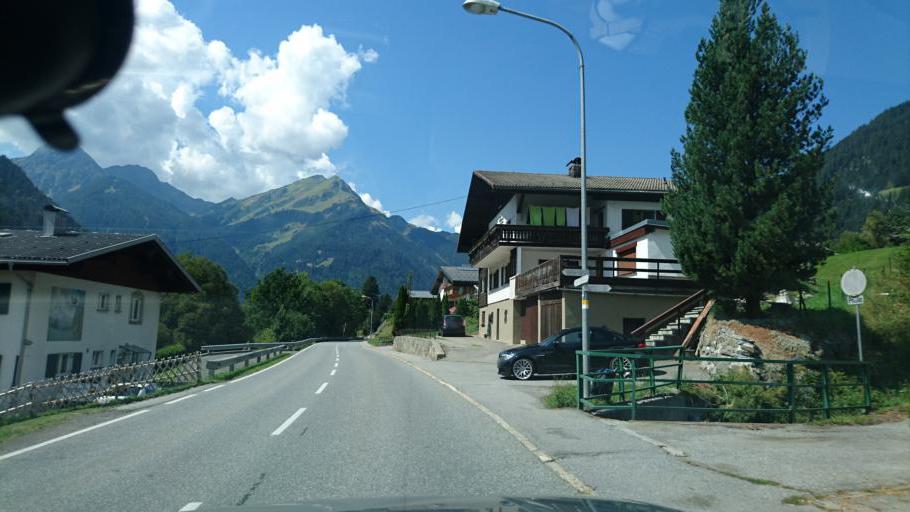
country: AT
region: Vorarlberg
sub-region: Politischer Bezirk Bludenz
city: Sankt Gallenkirch
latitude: 47.0185
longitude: 9.9862
